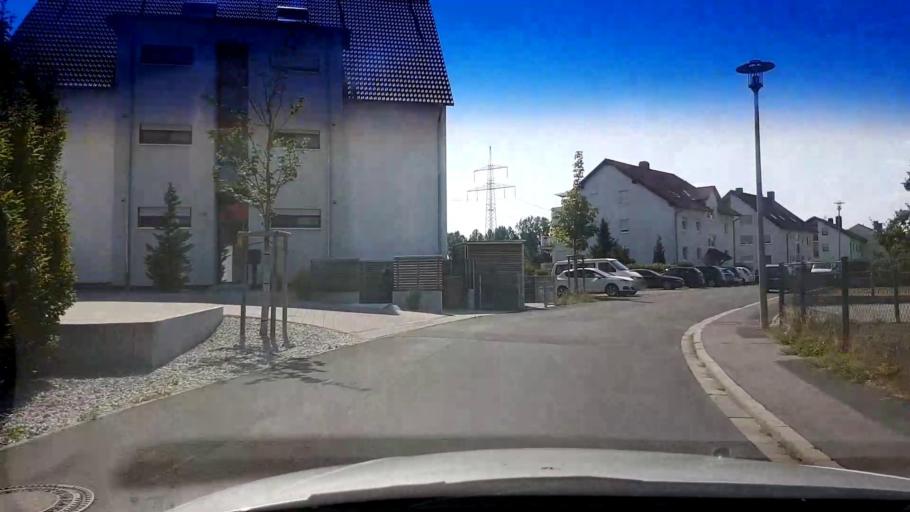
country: DE
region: Bavaria
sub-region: Upper Franconia
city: Hallstadt
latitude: 49.9296
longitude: 10.8620
